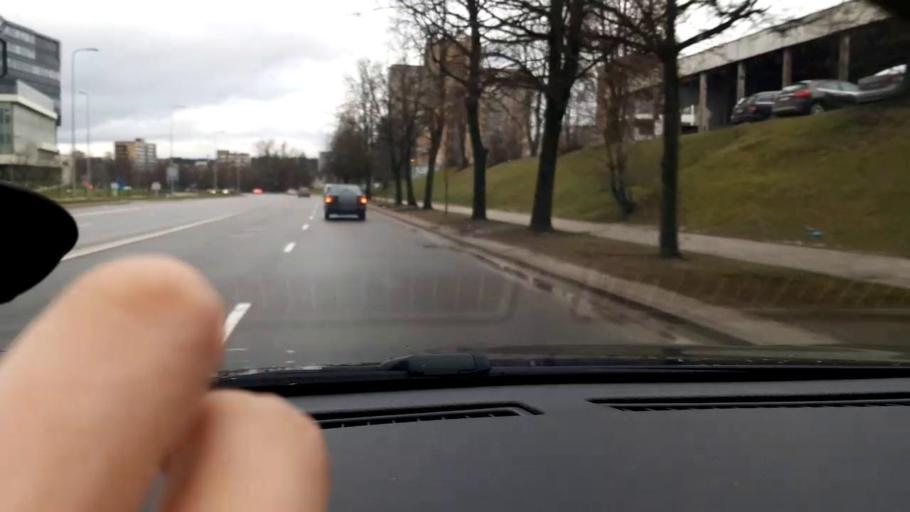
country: LT
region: Vilnius County
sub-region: Vilnius
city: Vilnius
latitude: 54.7182
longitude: 25.2867
